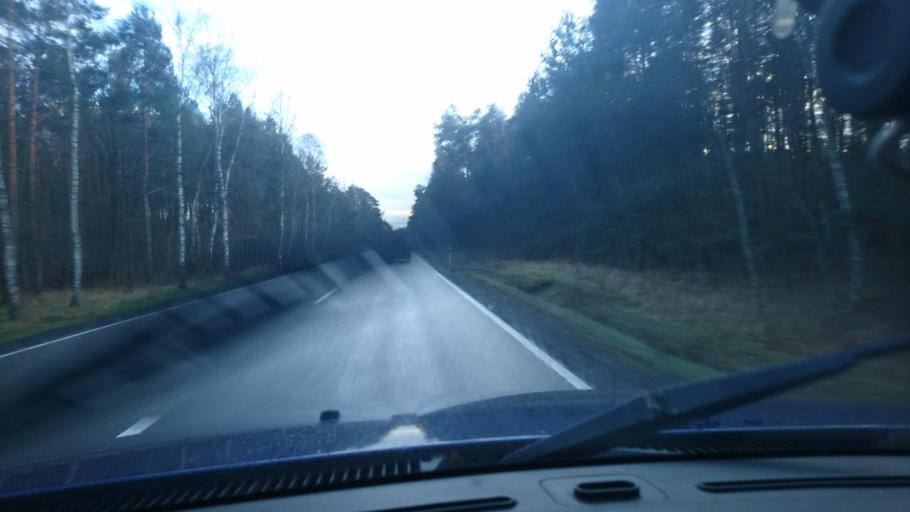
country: PL
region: Greater Poland Voivodeship
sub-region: Powiat kepinski
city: Bralin
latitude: 51.3450
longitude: 17.9511
